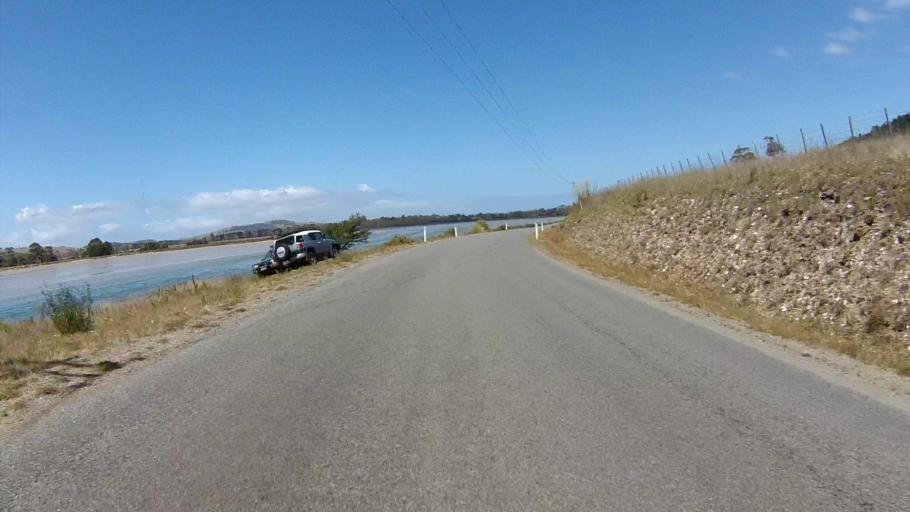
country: AU
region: Tasmania
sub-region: Clarence
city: Lauderdale
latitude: -42.9197
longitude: 147.4787
